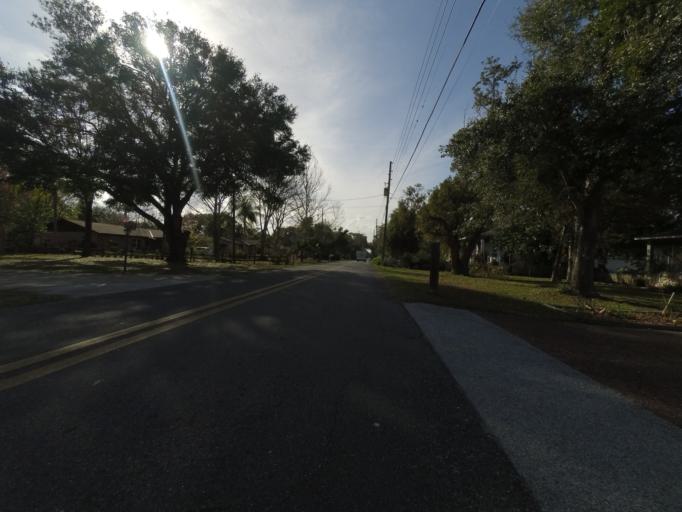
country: US
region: Florida
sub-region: Lake County
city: Eustis
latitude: 28.8287
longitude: -81.6715
